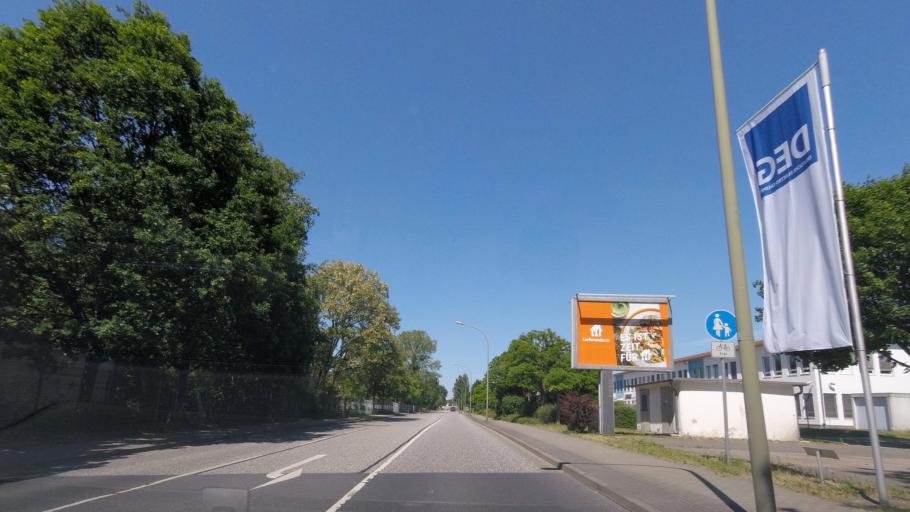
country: DE
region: Brandenburg
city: Potsdam
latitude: 52.3559
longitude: 13.1150
